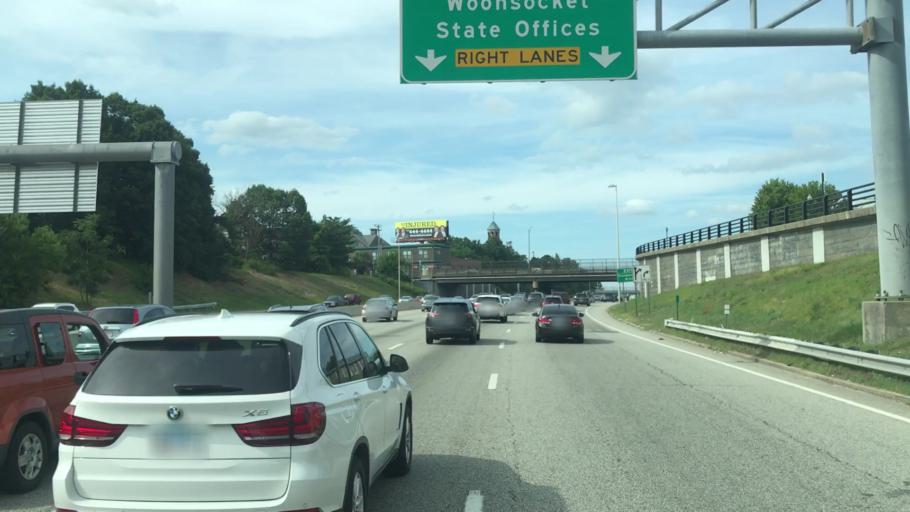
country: US
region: Rhode Island
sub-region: Providence County
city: Providence
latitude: 41.8302
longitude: -71.4176
